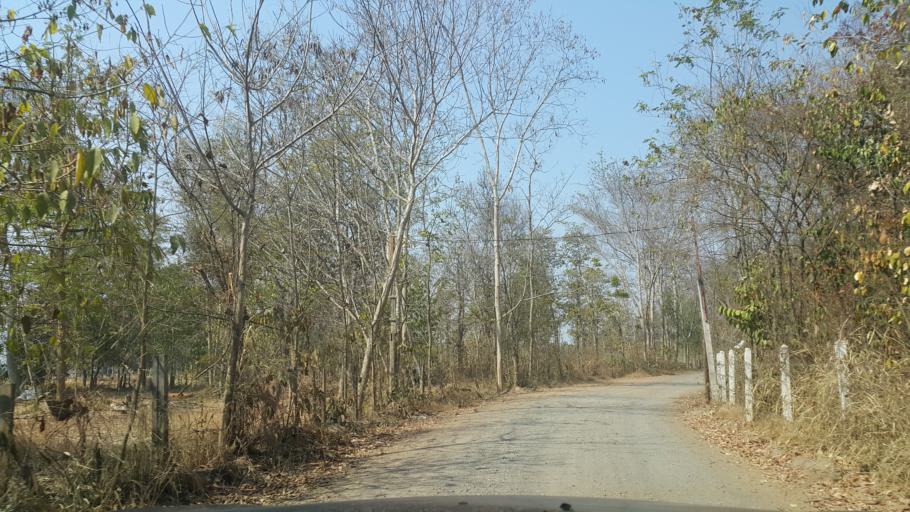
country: TH
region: Buriram
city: Krasang
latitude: 15.0922
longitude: 103.3728
